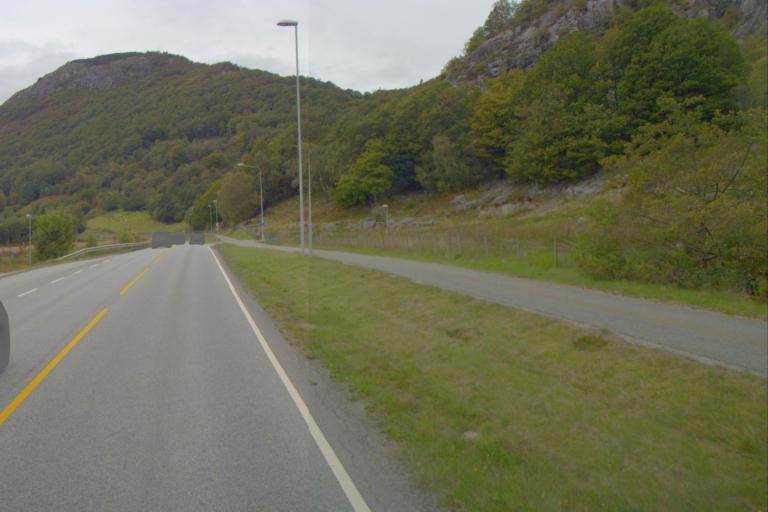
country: NO
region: Rogaland
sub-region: Sandnes
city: Hommersak
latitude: 58.8728
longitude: 5.8151
